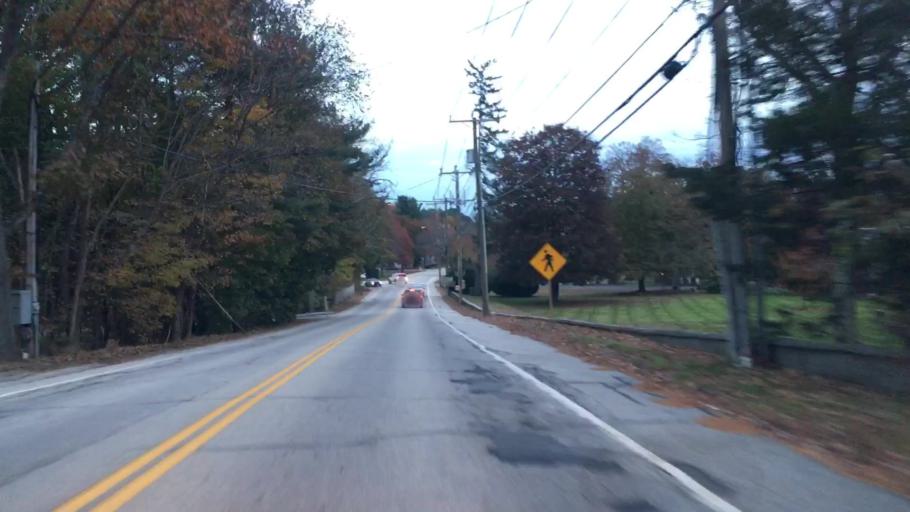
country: US
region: New Hampshire
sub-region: Hillsborough County
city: Milford
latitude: 42.8607
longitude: -71.6319
